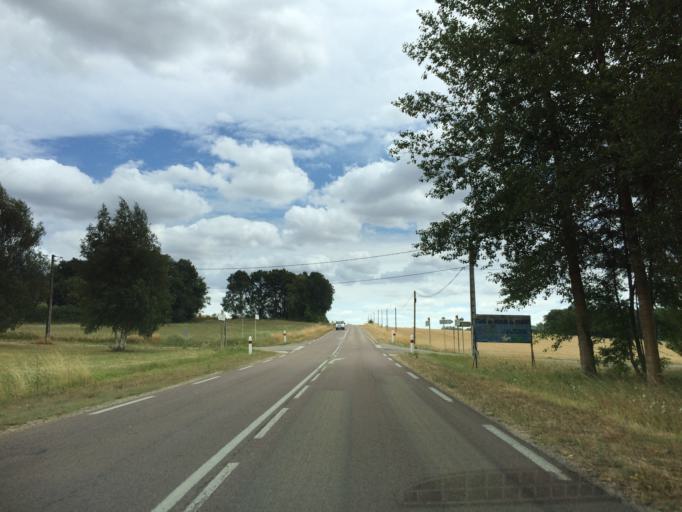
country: FR
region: Bourgogne
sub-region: Departement de l'Yonne
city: Fleury-la-Vallee
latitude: 47.8295
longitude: 3.4172
